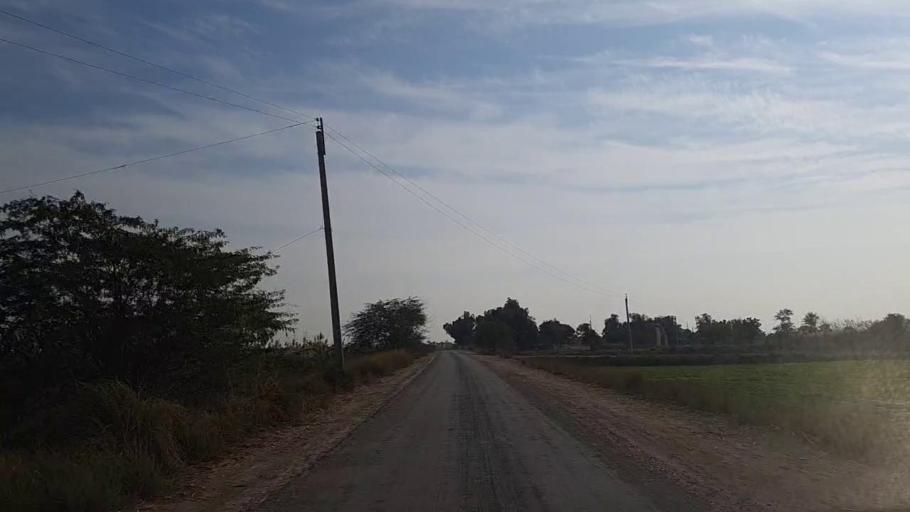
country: PK
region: Sindh
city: Daur
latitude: 26.4733
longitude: 68.4179
